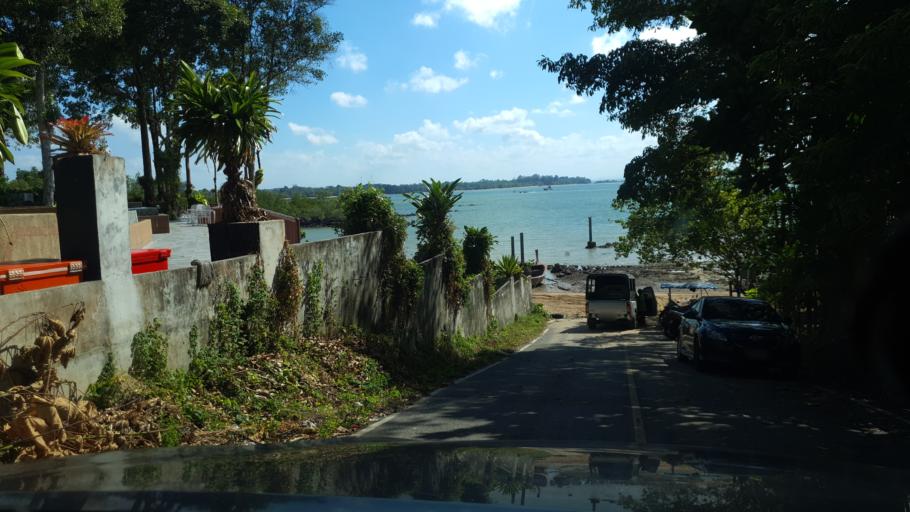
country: TH
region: Phangnga
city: Ban Ao Nang
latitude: 8.0246
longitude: 98.8557
